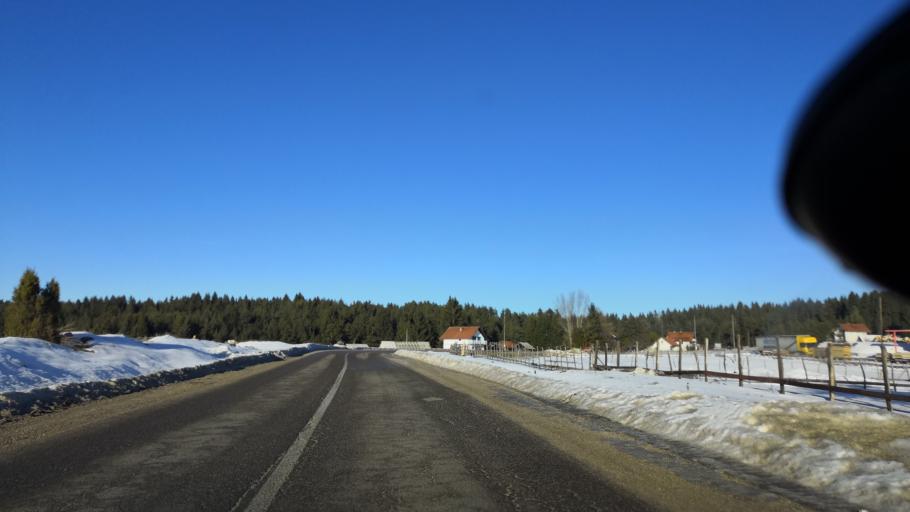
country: BA
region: Republika Srpska
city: Han Pijesak
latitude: 44.0370
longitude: 18.9271
